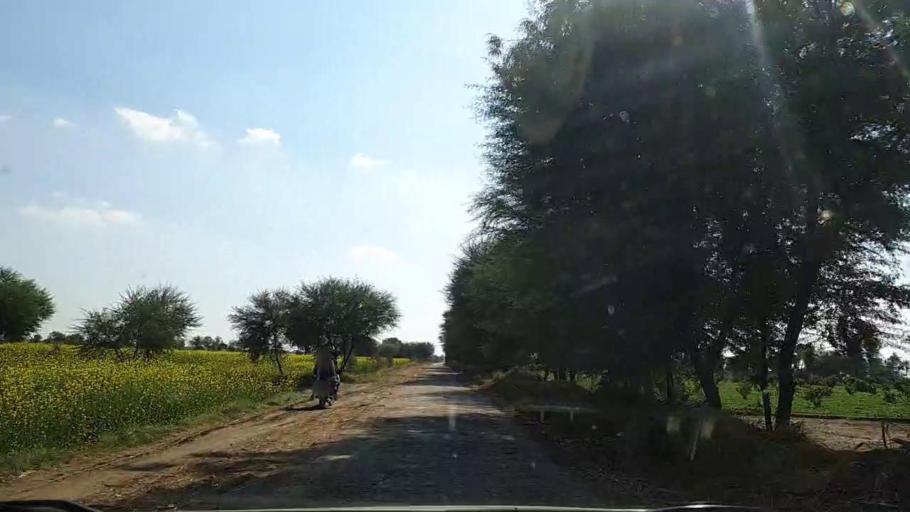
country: PK
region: Sindh
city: Pithoro
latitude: 25.6650
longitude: 69.4524
